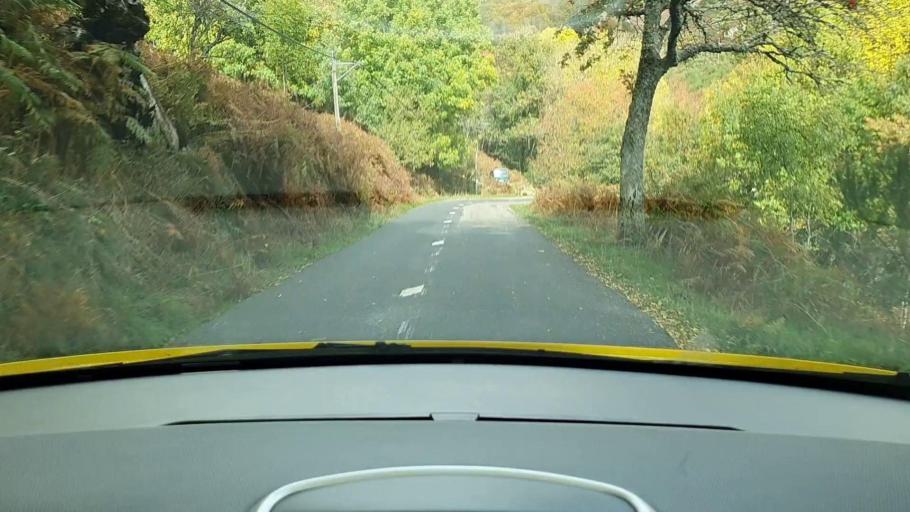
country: FR
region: Languedoc-Roussillon
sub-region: Departement de la Lozere
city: Meyrueis
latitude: 44.0755
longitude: 3.4802
